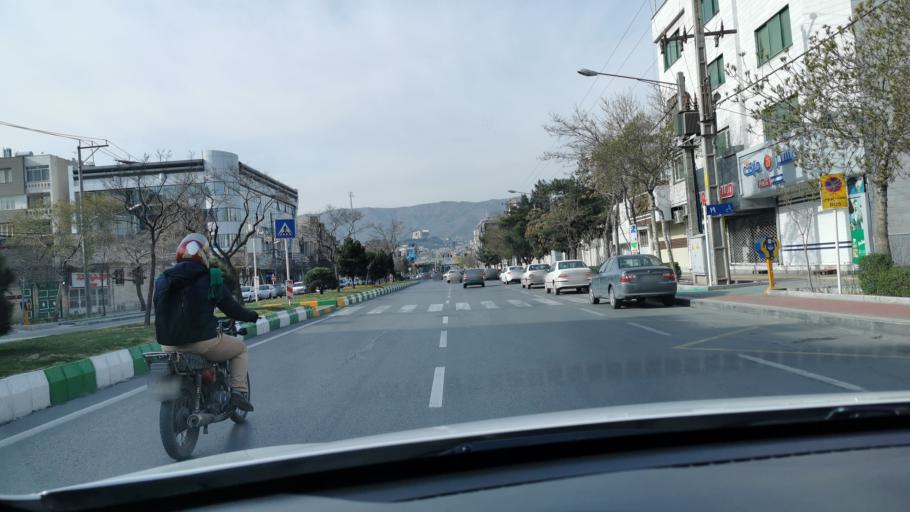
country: IR
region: Razavi Khorasan
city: Mashhad
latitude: 36.3173
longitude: 59.5102
